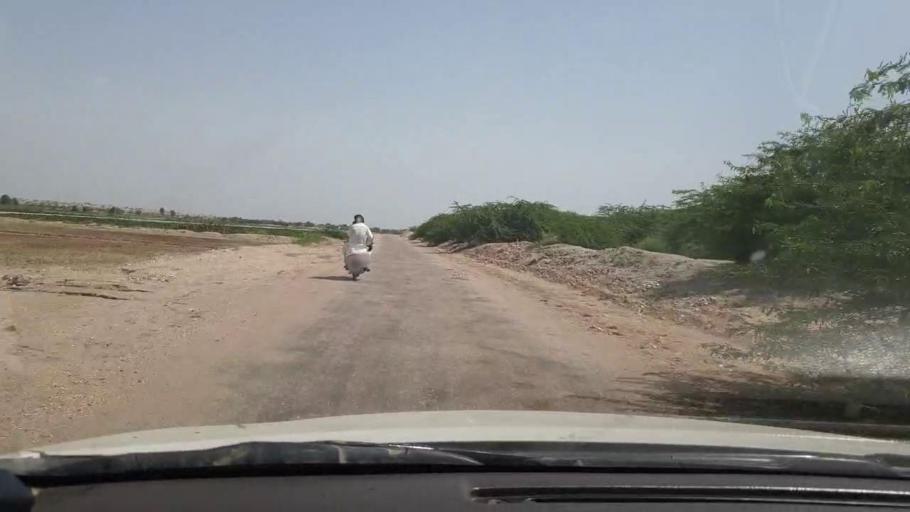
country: PK
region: Sindh
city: Rohri
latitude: 27.4879
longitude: 69.0538
